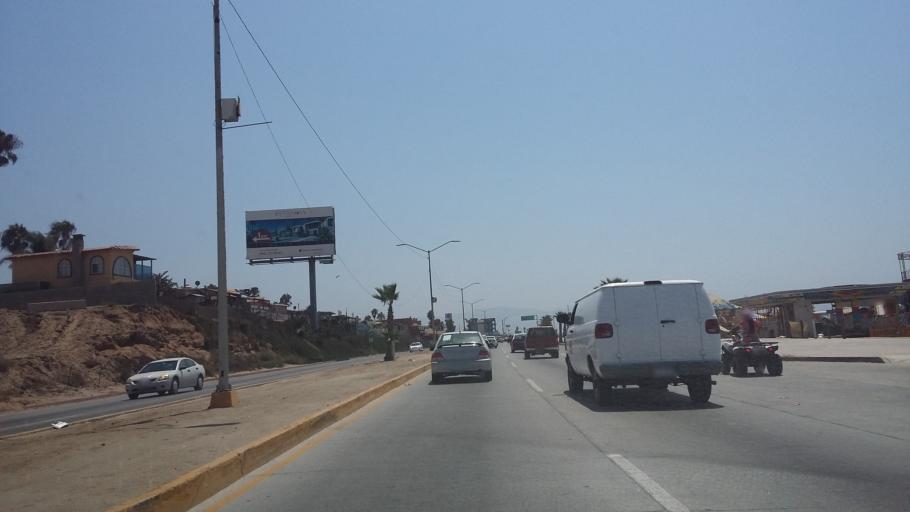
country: MX
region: Baja California
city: Ensenada
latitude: 31.8431
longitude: -116.6116
